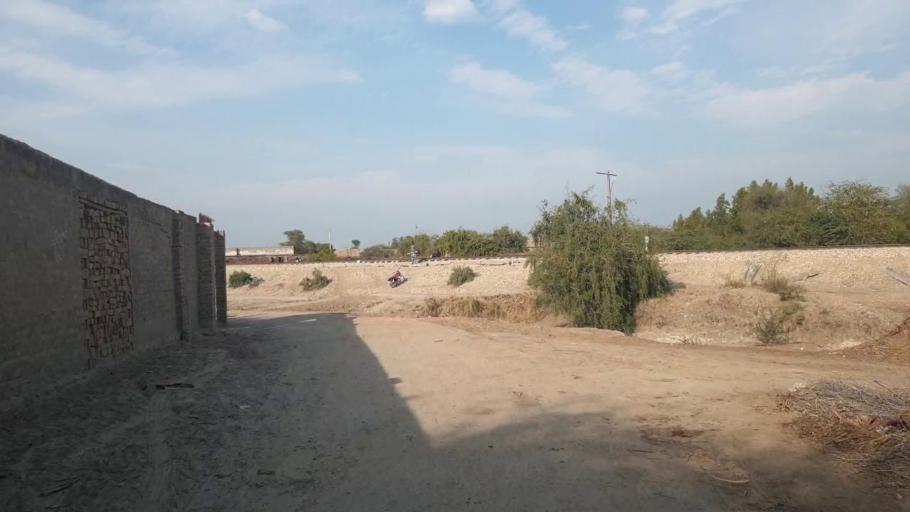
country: PK
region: Sindh
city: Shahdadpur
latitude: 26.0407
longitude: 68.5336
